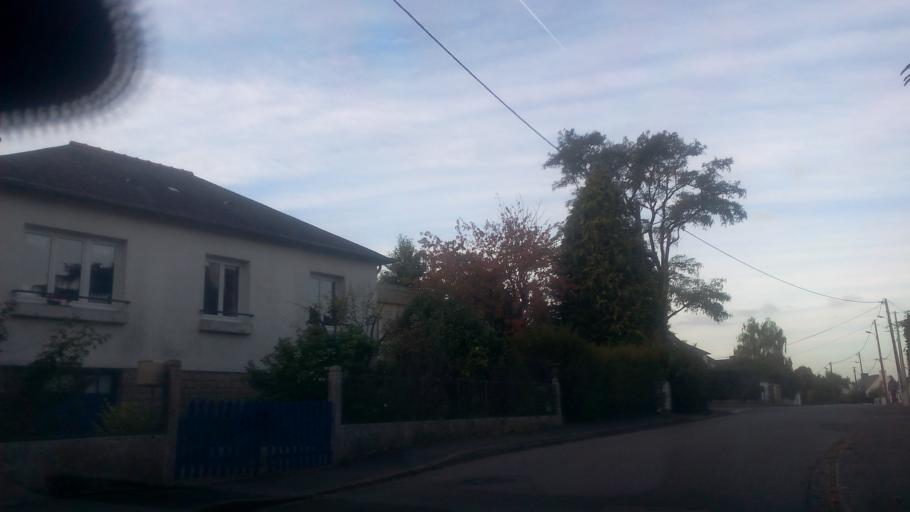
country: FR
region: Brittany
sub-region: Departement d'Ille-et-Vilaine
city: Redon
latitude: 47.6570
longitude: -2.0897
